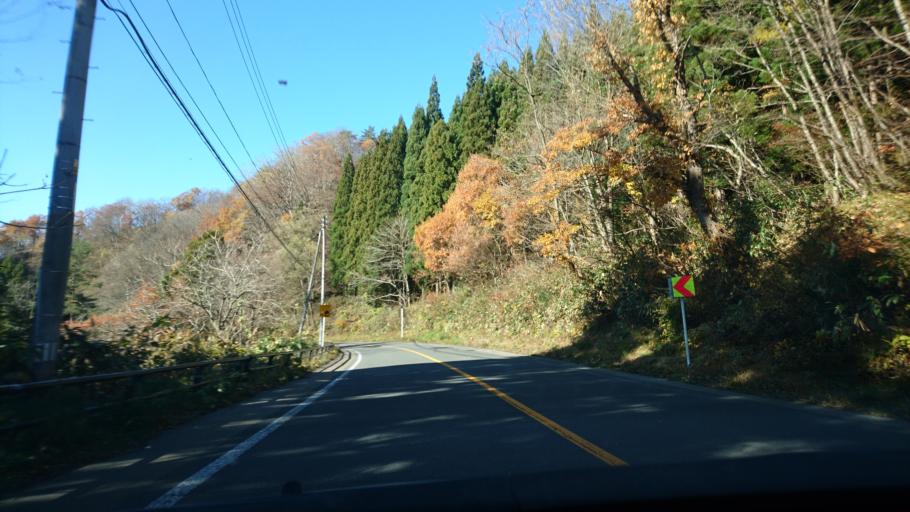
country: JP
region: Akita
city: Yokotemachi
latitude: 39.2823
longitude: 140.6729
